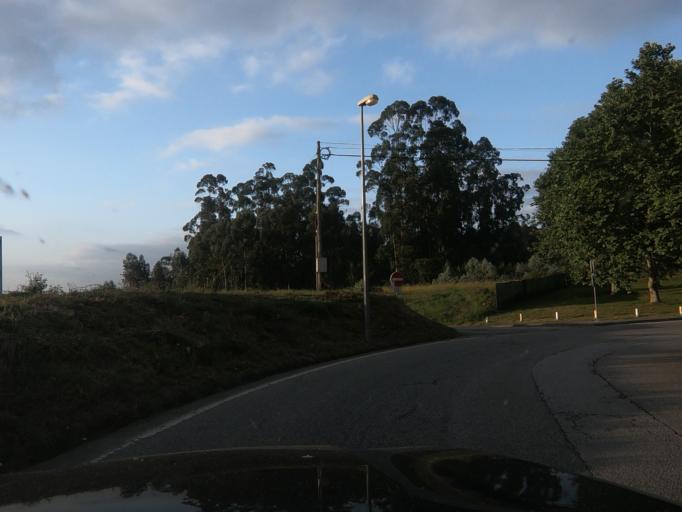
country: PT
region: Aveiro
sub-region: Estarreja
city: Beduido
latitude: 40.7566
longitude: -8.5354
